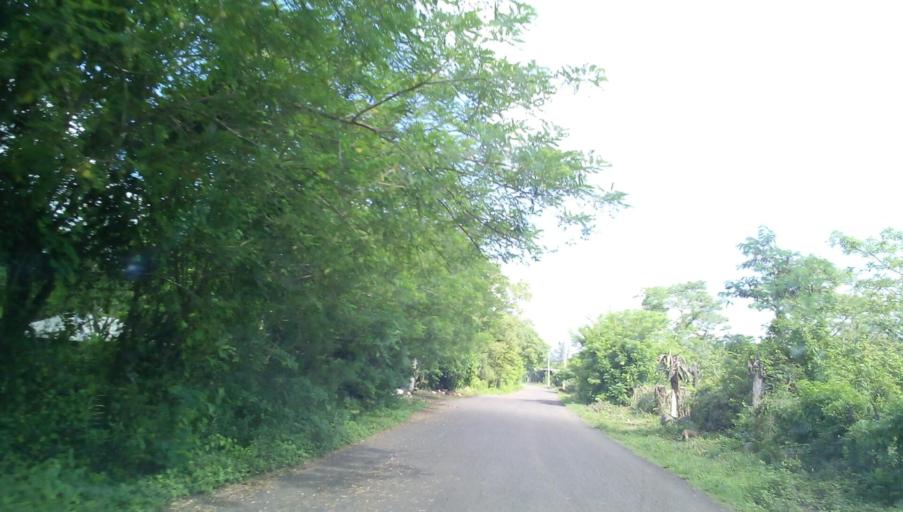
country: MX
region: Veracruz
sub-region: Citlaltepetl
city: Las Sabinas
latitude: 21.3668
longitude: -97.9007
